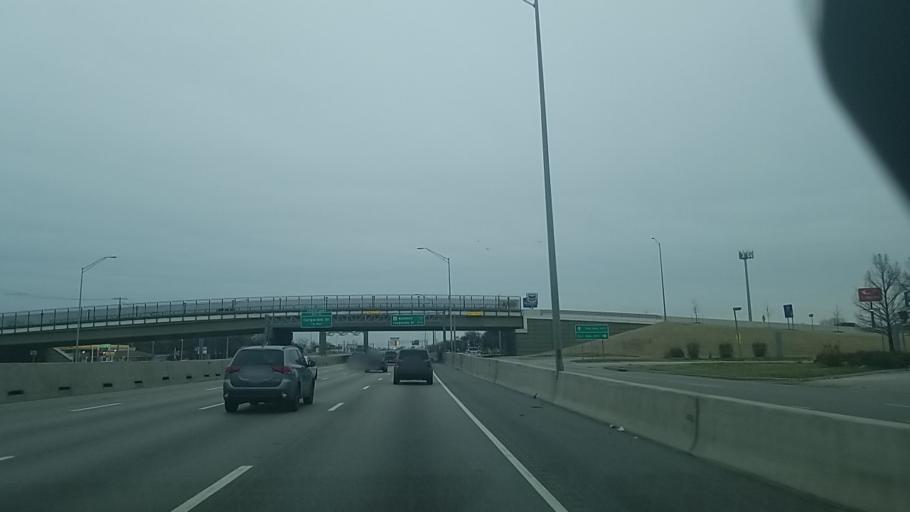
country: US
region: Texas
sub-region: Denton County
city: Lewisville
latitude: 33.0390
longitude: -97.0031
